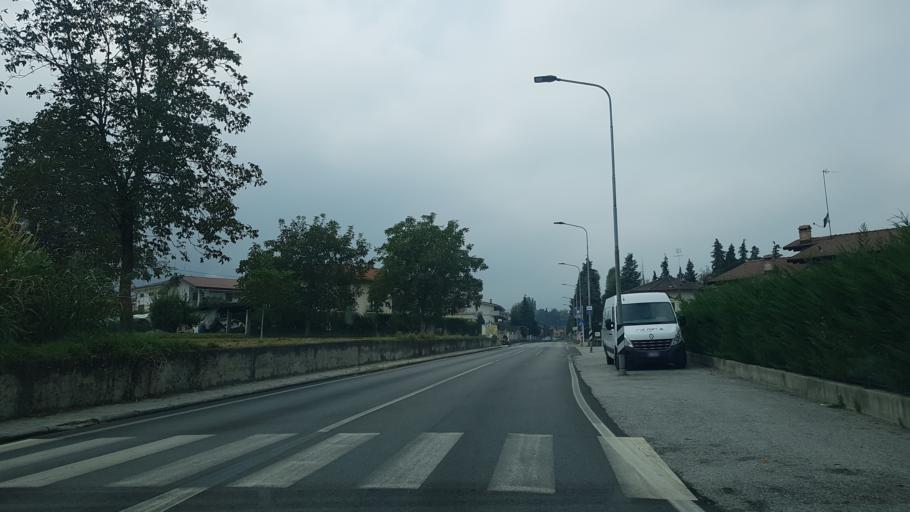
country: IT
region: Piedmont
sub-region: Provincia di Cuneo
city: Peveragno
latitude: 44.3302
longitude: 7.6257
